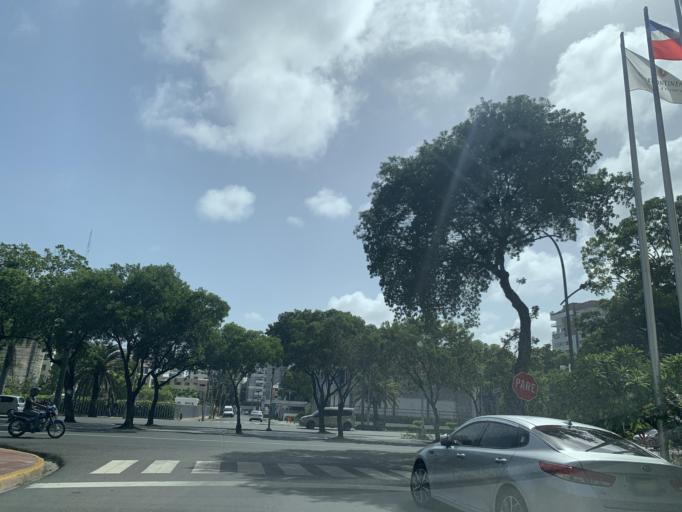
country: DO
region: Nacional
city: La Julia
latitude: 18.4682
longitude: -69.9387
